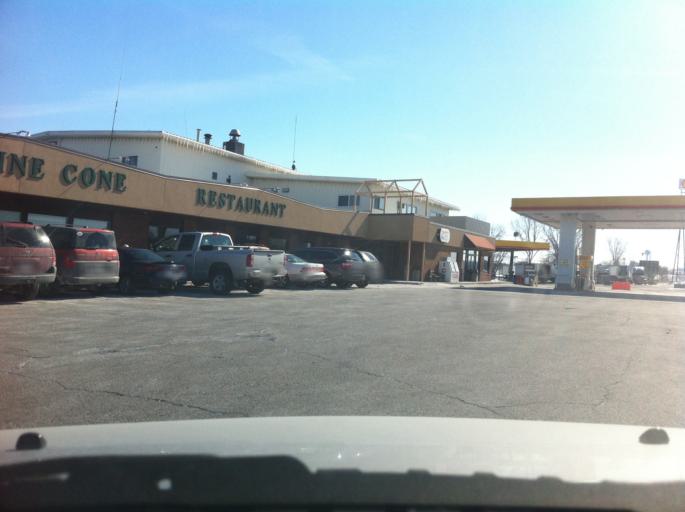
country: US
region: Wisconsin
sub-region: Dane County
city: Windsor
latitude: 43.1818
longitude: -89.3240
